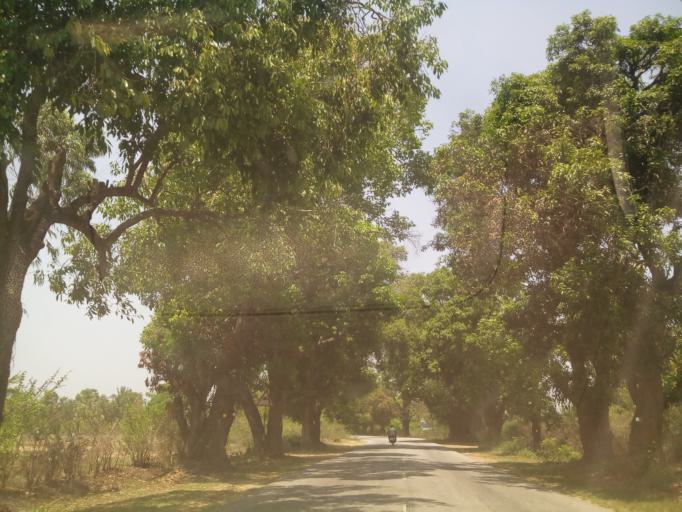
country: IN
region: Karnataka
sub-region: Hassan
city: Alur
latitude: 12.9506
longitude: 75.9292
